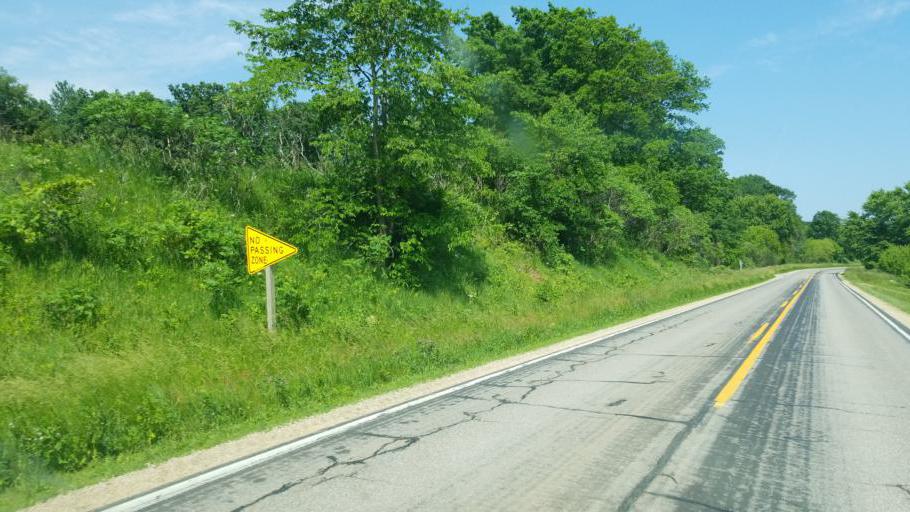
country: US
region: Wisconsin
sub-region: Vernon County
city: Hillsboro
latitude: 43.6452
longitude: -90.4233
